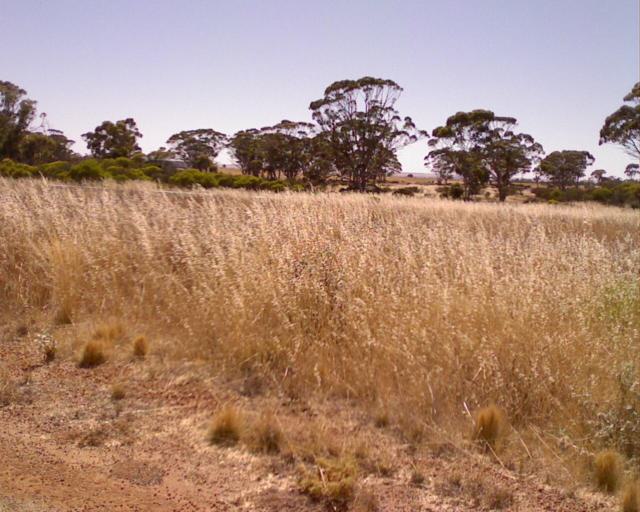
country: AU
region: Western Australia
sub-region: Wongan-Ballidu
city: Wongan Hills
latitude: -30.3914
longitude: 116.6691
